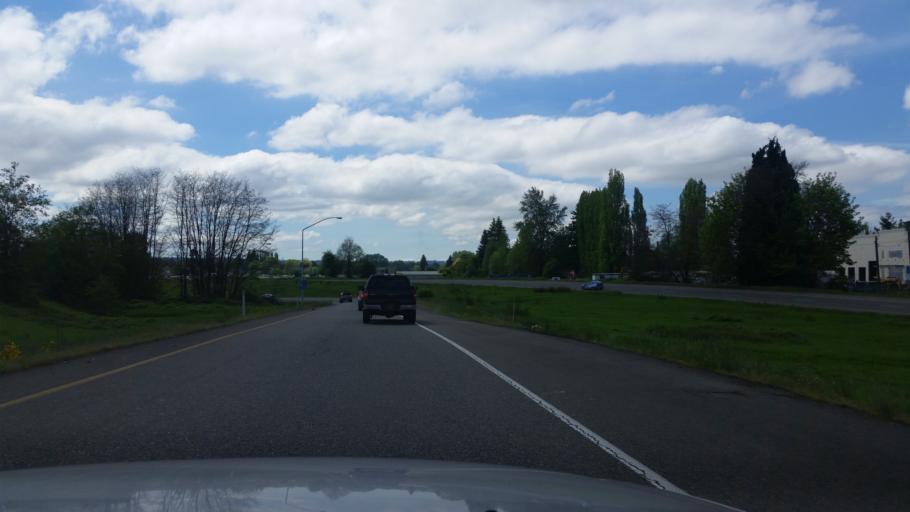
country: US
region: Washington
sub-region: Pierce County
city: Sumner
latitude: 47.2023
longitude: -122.2590
